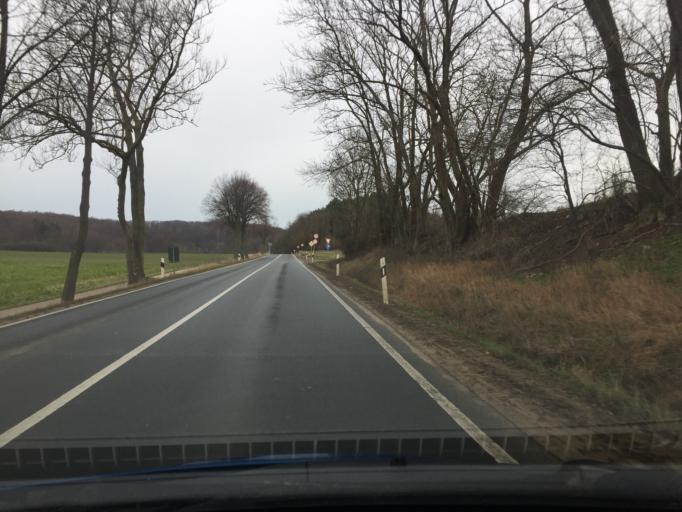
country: DE
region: Lower Saxony
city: Weenzen
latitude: 52.0273
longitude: 9.6758
